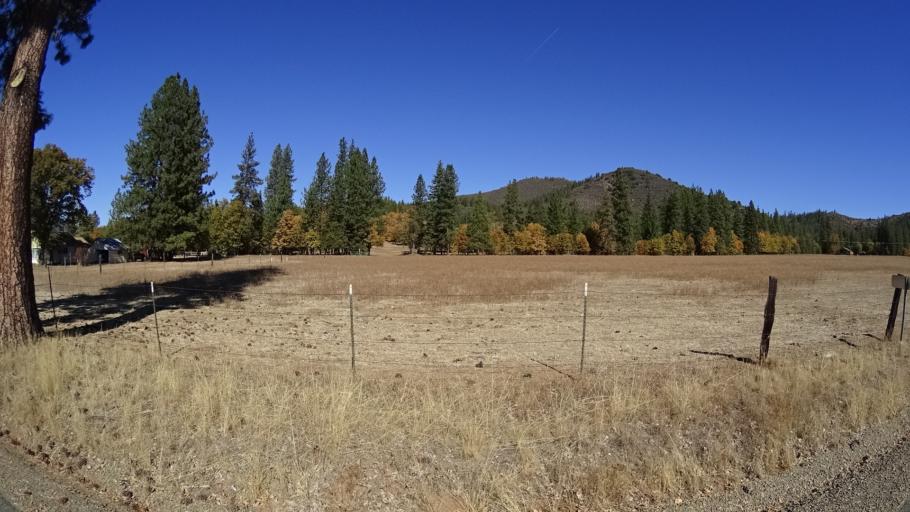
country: US
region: California
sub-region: Siskiyou County
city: Yreka
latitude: 41.5723
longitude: -122.9495
